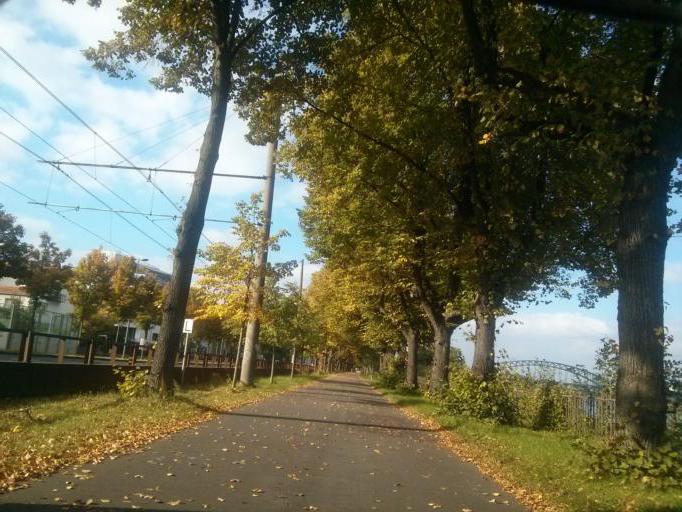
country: DE
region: North Rhine-Westphalia
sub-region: Regierungsbezirk Koln
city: Bayenthal
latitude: 50.9099
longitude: 6.9752
